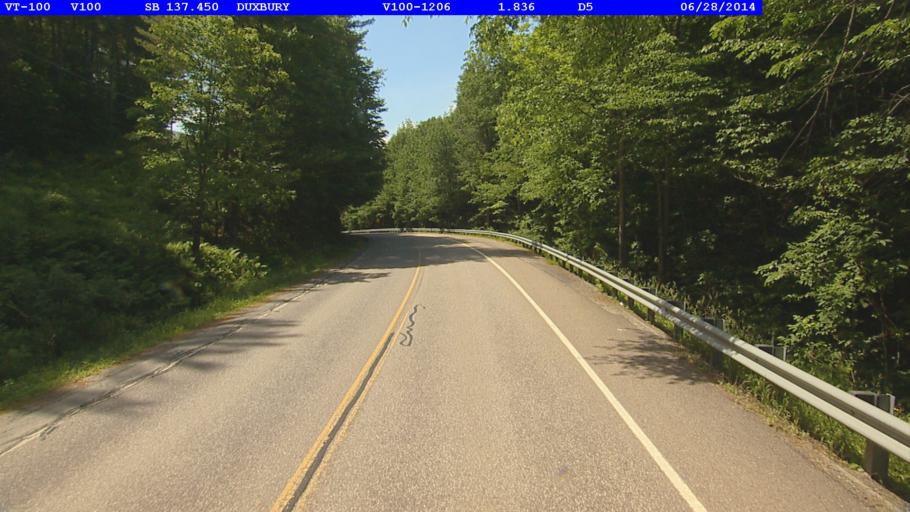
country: US
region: Vermont
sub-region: Washington County
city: Waterbury
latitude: 44.2723
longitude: -72.7854
